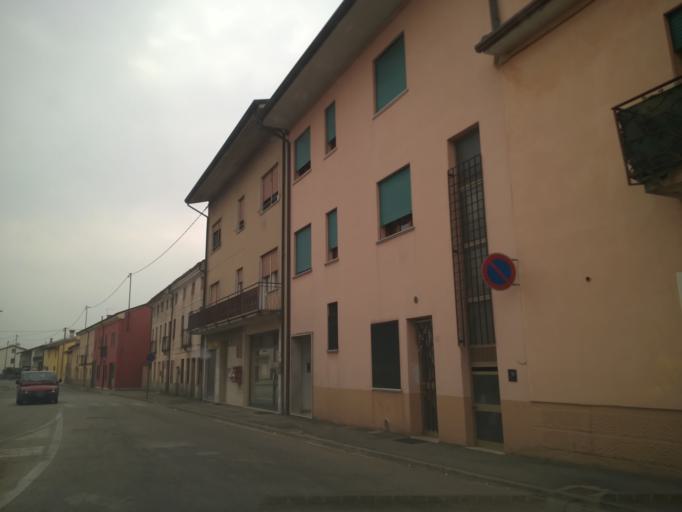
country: IT
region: Veneto
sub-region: Provincia di Vicenza
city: Poianella
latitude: 45.6328
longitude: 11.6259
